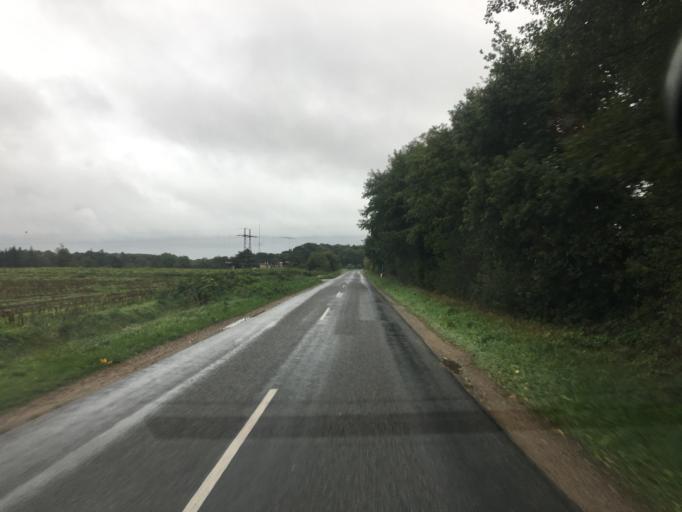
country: DE
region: Schleswig-Holstein
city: Bramstedtlund
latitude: 54.9619
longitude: 9.0509
